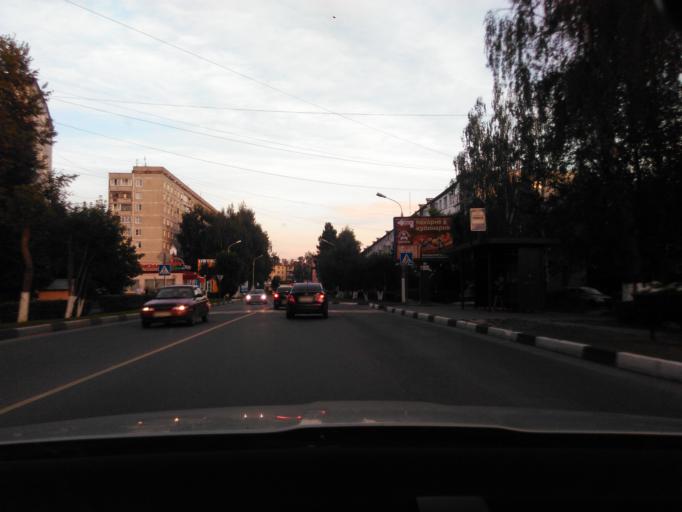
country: RU
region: Moskovskaya
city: Klin
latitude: 56.3219
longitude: 36.7214
